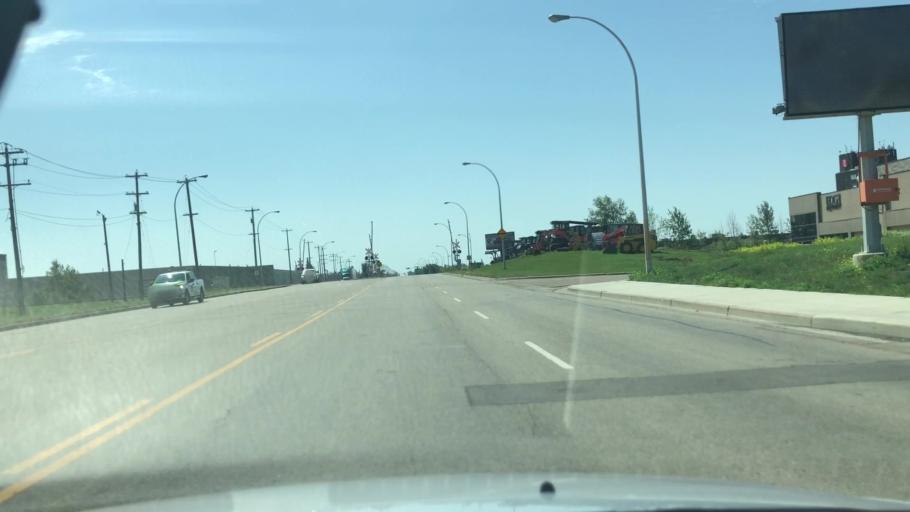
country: CA
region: Alberta
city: St. Albert
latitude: 53.5845
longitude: -113.5781
